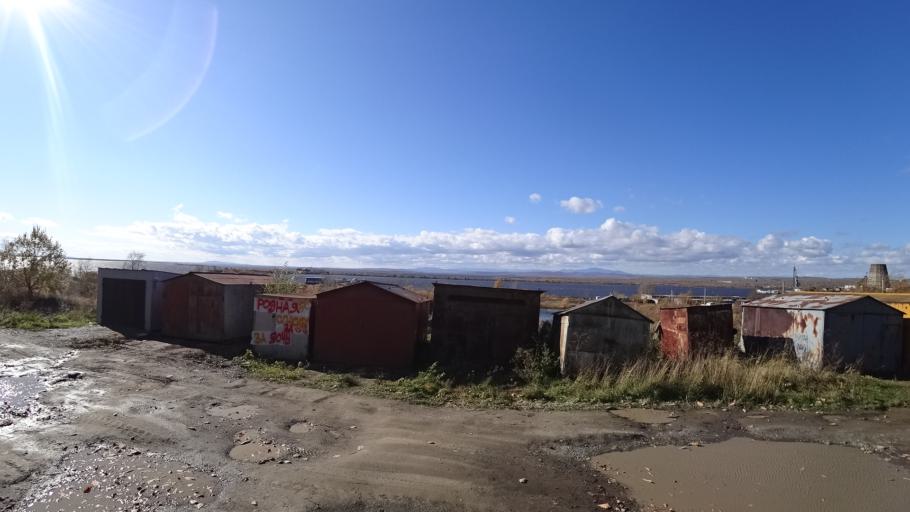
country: RU
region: Khabarovsk Krai
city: Amursk
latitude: 50.2164
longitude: 136.8890
